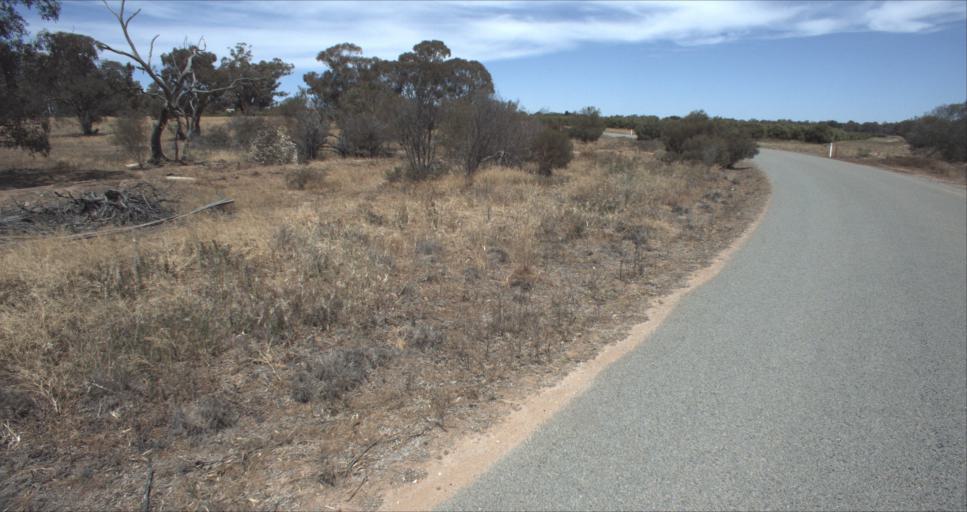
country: AU
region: New South Wales
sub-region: Leeton
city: Leeton
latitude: -34.6739
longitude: 146.4334
